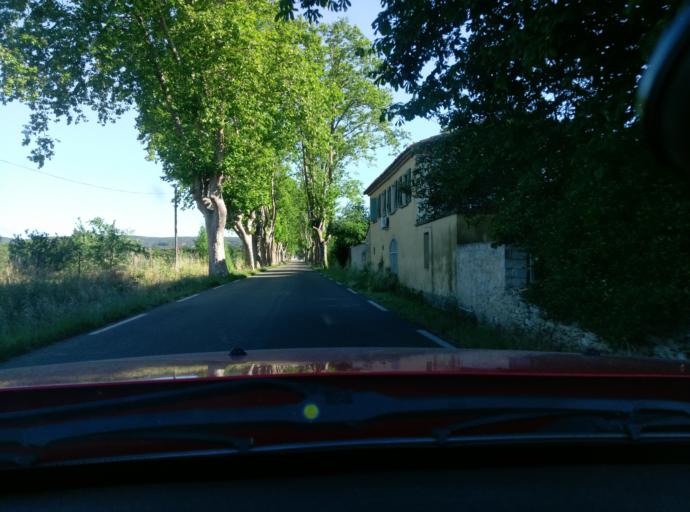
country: FR
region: Languedoc-Roussillon
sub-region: Departement du Gard
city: Uzes
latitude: 44.0410
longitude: 4.4071
